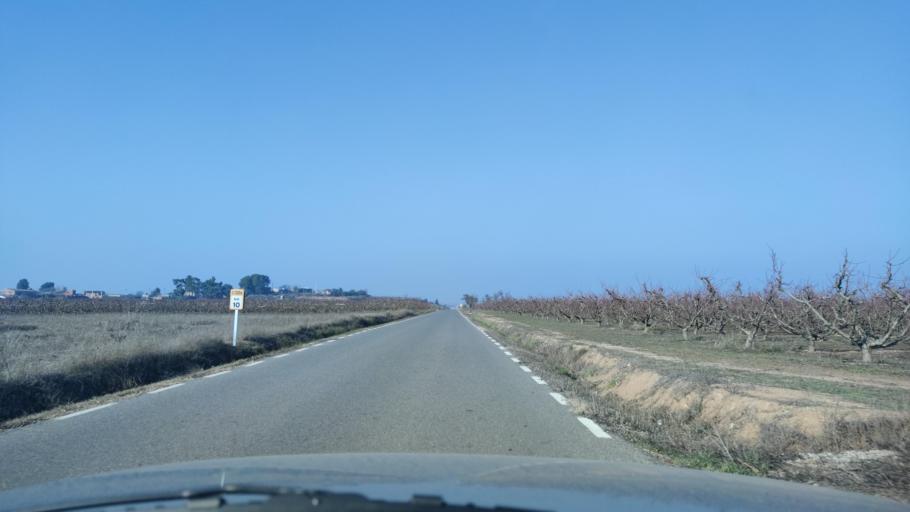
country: ES
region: Catalonia
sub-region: Provincia de Lleida
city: Sunyer
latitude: 41.5505
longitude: 0.5741
